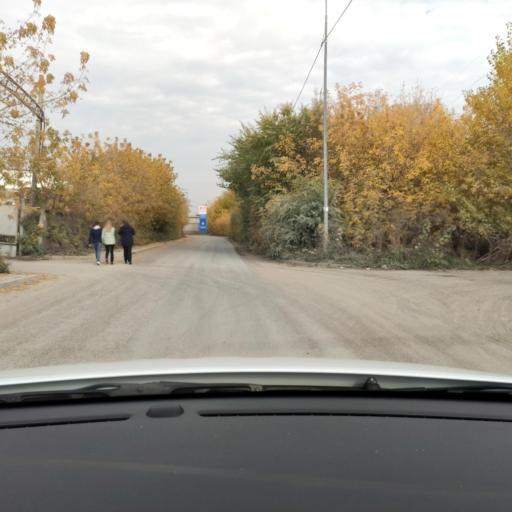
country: RU
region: Tatarstan
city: Verkhniy Uslon
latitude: 55.8025
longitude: 49.0467
